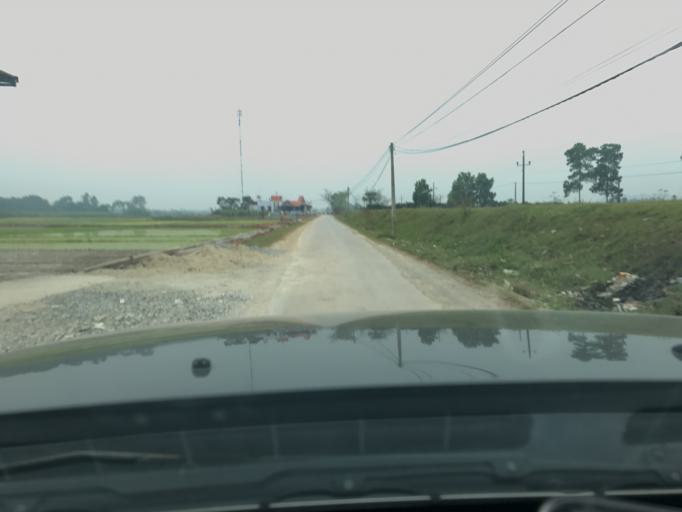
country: VN
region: Thanh Hoa
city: Thi Tran Vinh Loc
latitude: 20.0264
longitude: 105.5456
